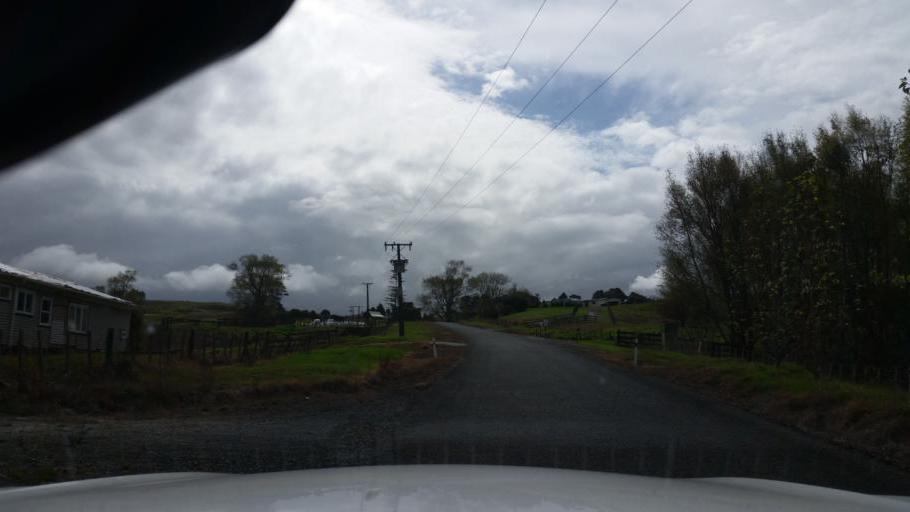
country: NZ
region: Northland
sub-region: Whangarei
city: Ruakaka
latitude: -36.1095
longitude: 174.2776
